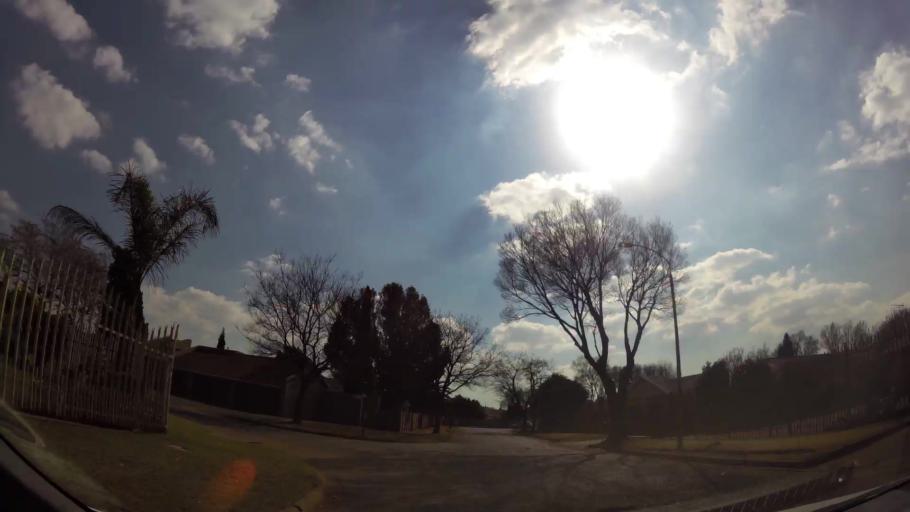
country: ZA
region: Gauteng
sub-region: Ekurhuleni Metropolitan Municipality
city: Germiston
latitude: -26.1928
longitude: 28.2078
